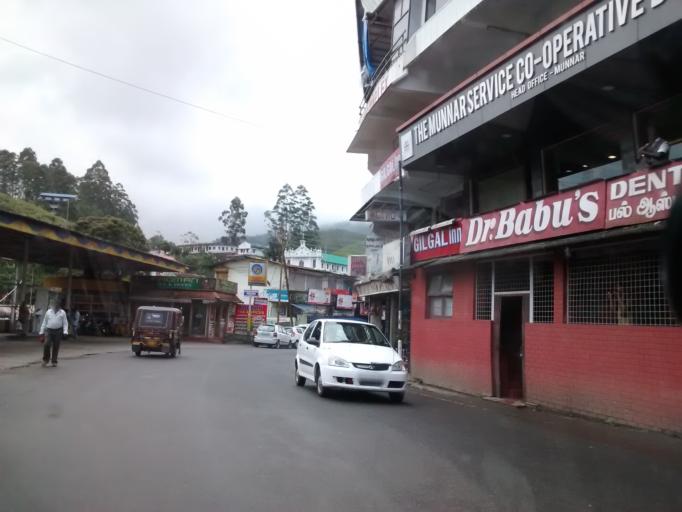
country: IN
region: Kerala
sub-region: Idukki
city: Munnar
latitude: 10.0862
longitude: 77.0608
